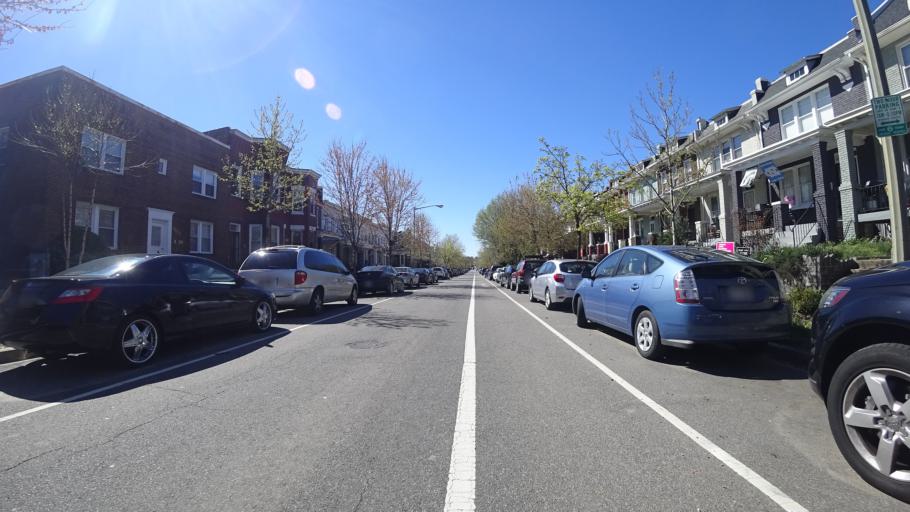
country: US
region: Washington, D.C.
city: Washington, D.C.
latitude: 38.9053
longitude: -77.0005
